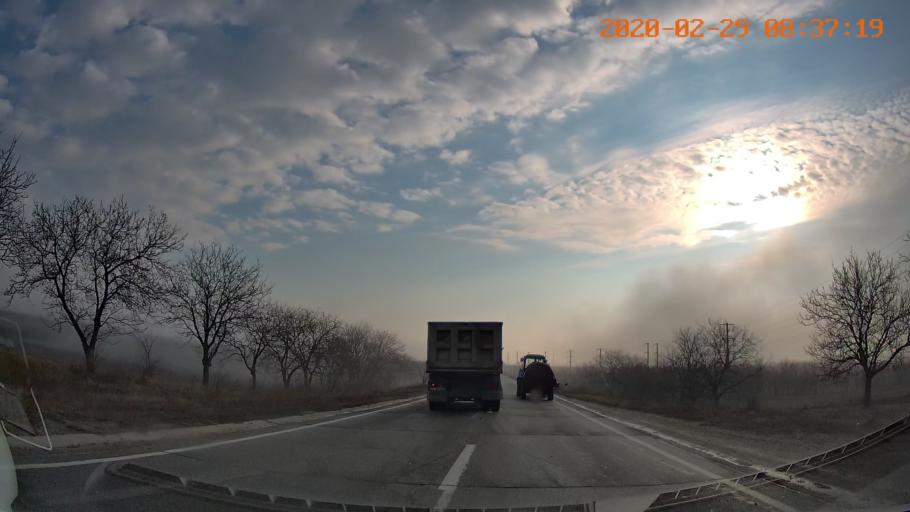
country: MD
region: Anenii Noi
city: Varnita
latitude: 46.9212
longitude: 29.3586
